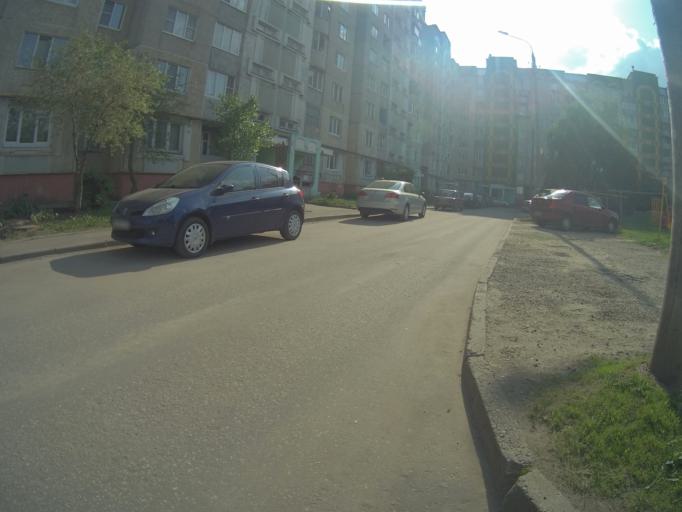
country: RU
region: Vladimir
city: Kommunar
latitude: 56.1681
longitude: 40.4476
